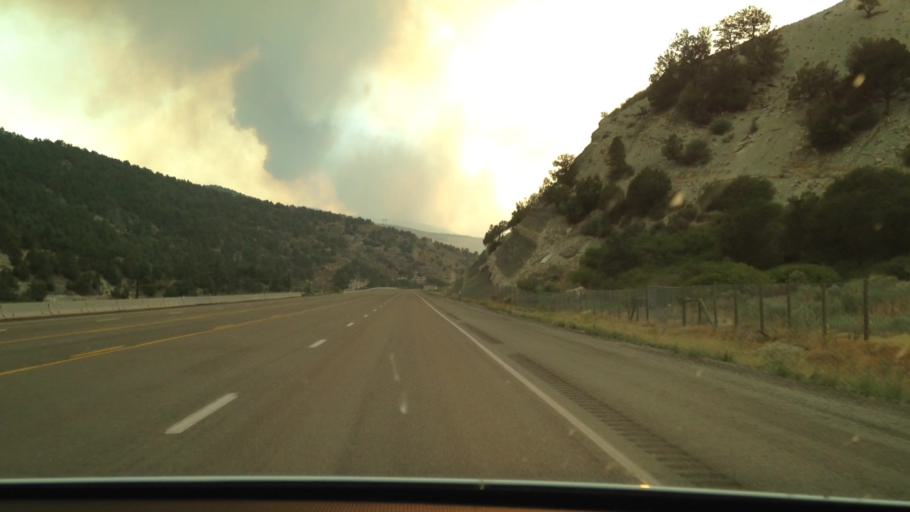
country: US
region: Utah
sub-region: Utah County
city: Mapleton
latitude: 39.9556
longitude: -111.2540
